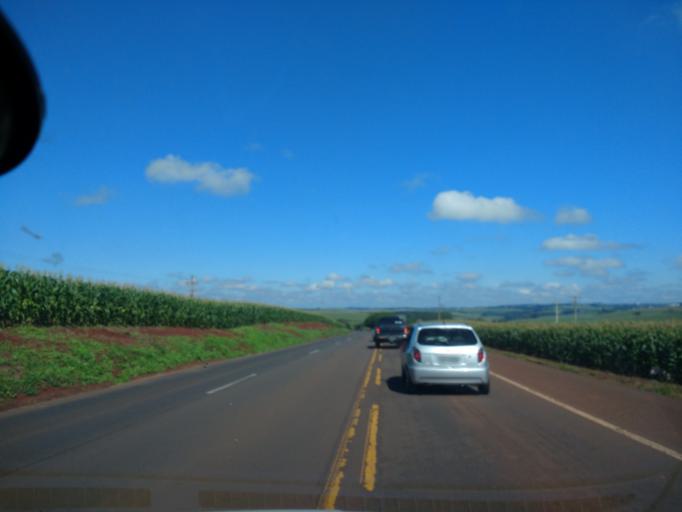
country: BR
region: Parana
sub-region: Cianorte
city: Cianorte
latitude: -23.6459
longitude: -52.4849
